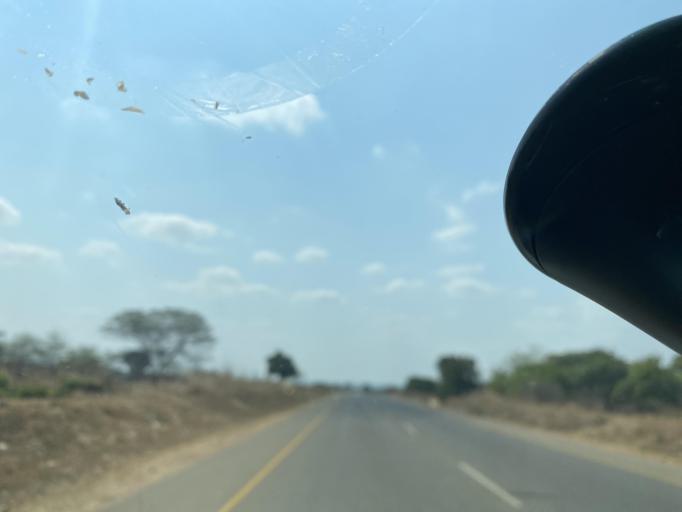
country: ZM
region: Lusaka
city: Chongwe
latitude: -15.5903
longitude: 28.7129
